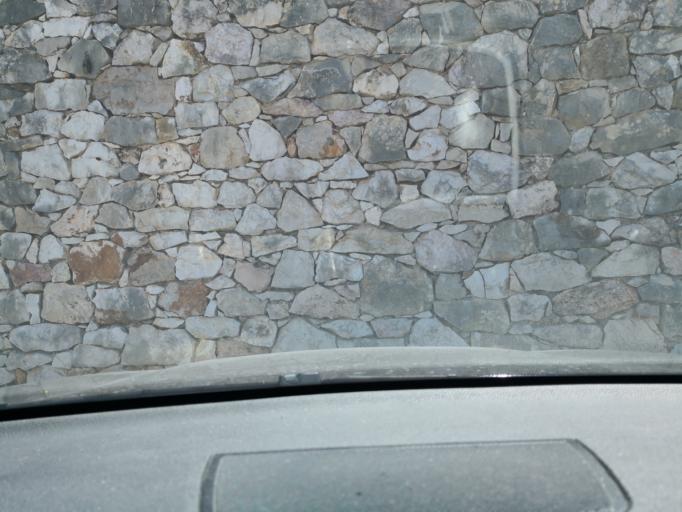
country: PT
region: Faro
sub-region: Loule
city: Vilamoura
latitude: 37.1040
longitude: -8.1161
